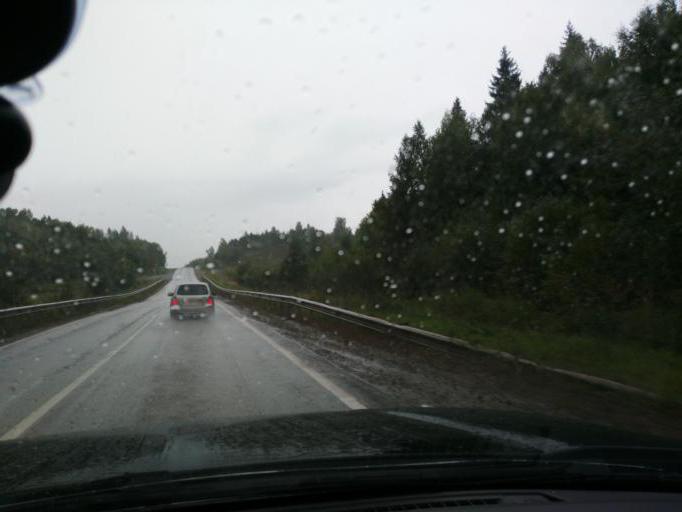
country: RU
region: Perm
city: Barda
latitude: 56.9153
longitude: 55.6802
